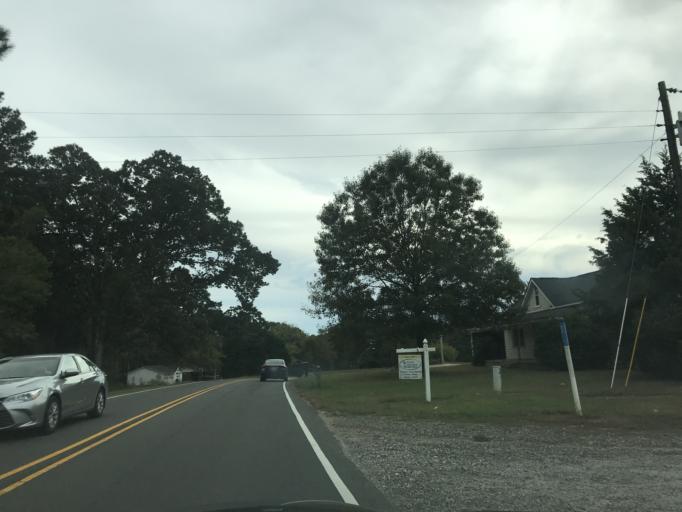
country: US
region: North Carolina
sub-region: Wake County
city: Rolesville
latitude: 35.9239
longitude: -78.5042
